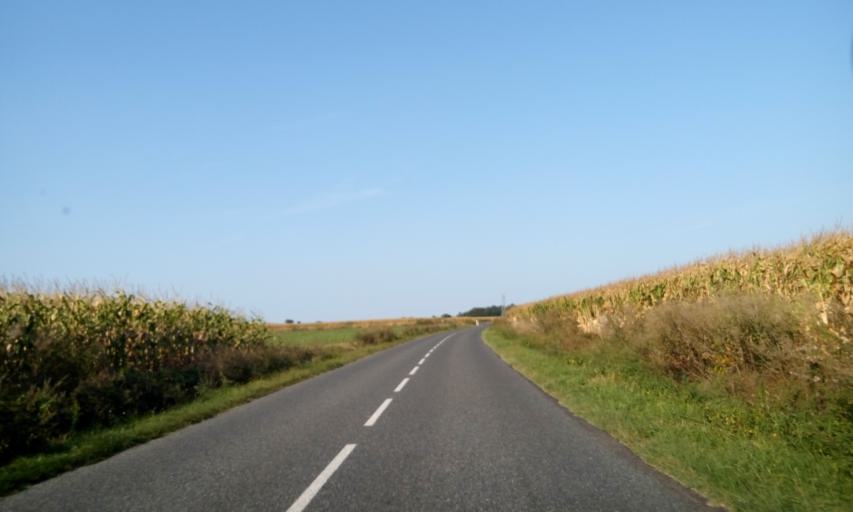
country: FR
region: Rhone-Alpes
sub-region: Departement de l'Ain
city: Saint-Didier-de-Formans
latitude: 45.9687
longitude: 4.7778
